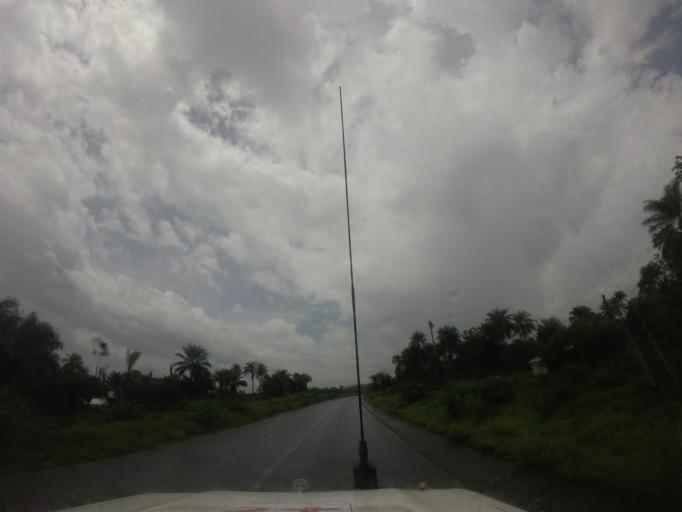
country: SL
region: Northern Province
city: Port Loko
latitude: 8.4886
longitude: -12.7793
